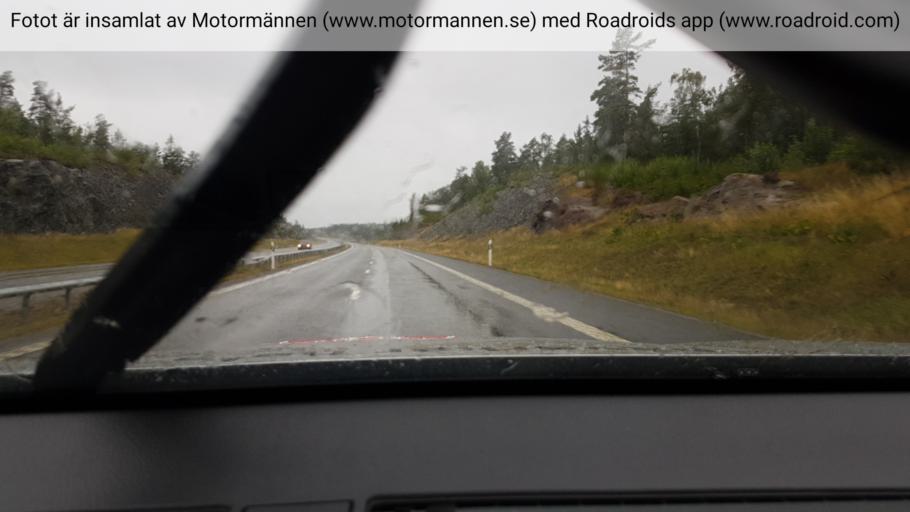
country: SE
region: Stockholm
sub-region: Nynashamns Kommun
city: Osmo
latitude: 59.0438
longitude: 17.9777
